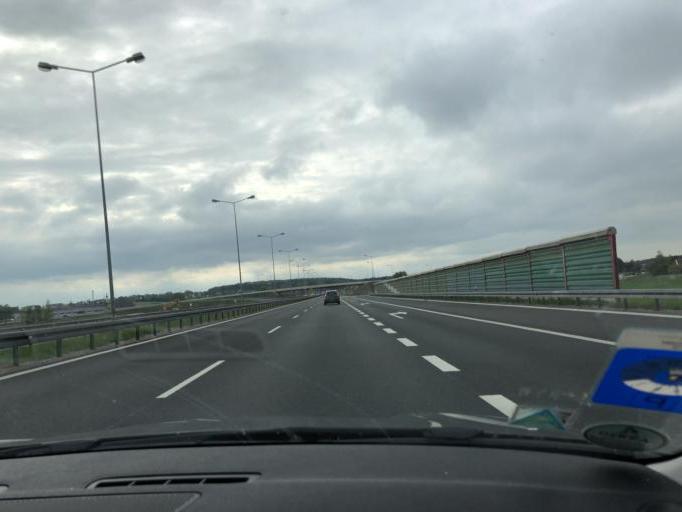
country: PL
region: Opole Voivodeship
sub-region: Powiat krapkowicki
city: Gogolin
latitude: 50.4861
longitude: 17.9983
